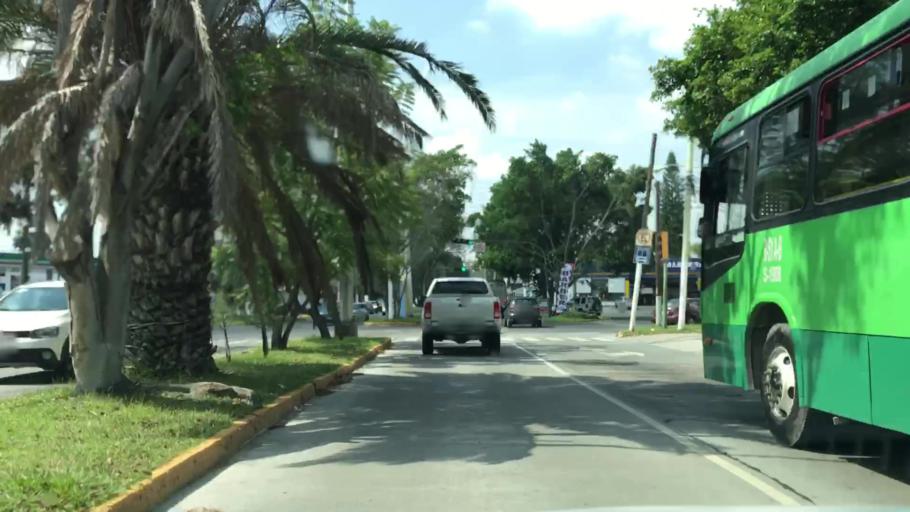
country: MX
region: Jalisco
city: Guadalajara
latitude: 20.6595
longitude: -103.4124
